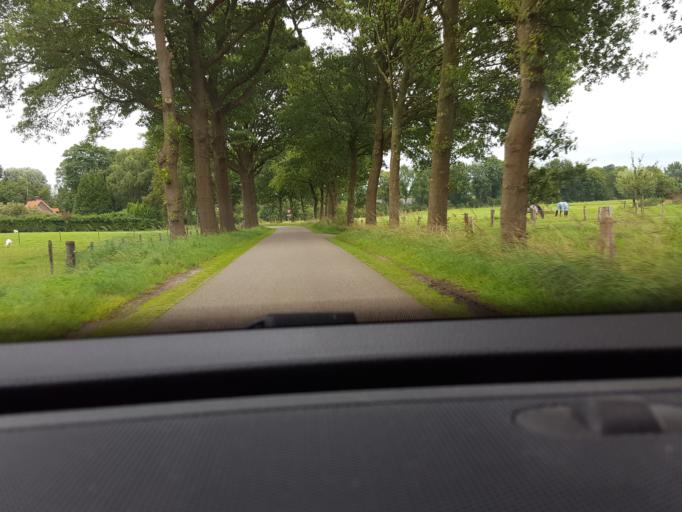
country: NL
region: Gelderland
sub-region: Gemeente Lochem
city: Almen
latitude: 52.1094
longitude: 6.2952
